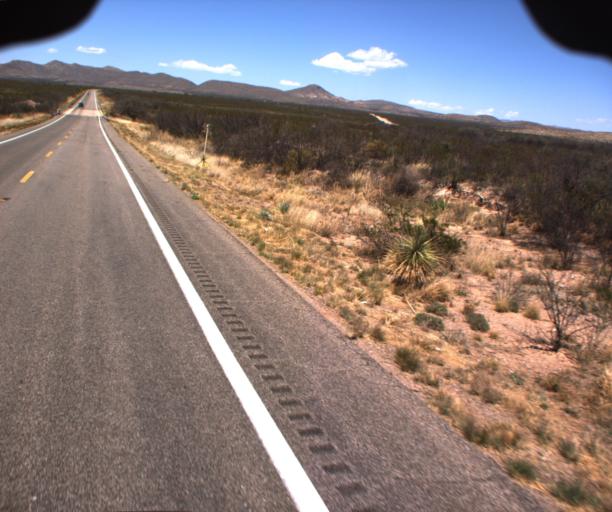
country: US
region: Arizona
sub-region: Cochise County
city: Tombstone
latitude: 31.6080
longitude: -110.0497
